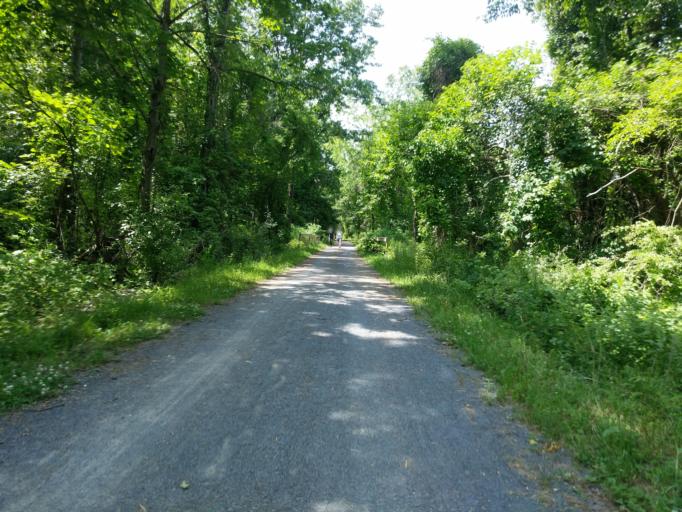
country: US
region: New York
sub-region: Tompkins County
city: Northwest Ithaca
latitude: 42.5078
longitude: -76.5529
